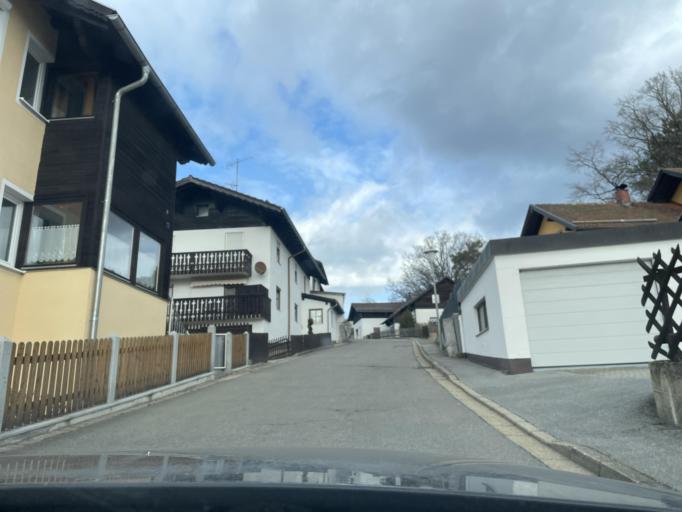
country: DE
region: Bavaria
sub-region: Lower Bavaria
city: Viechtach
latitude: 49.0858
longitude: 12.9055
